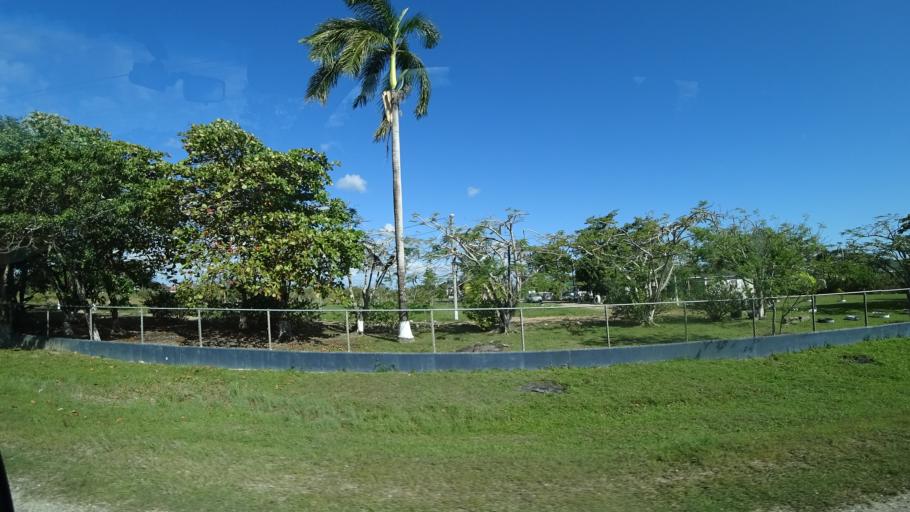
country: BZ
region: Belize
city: Belize City
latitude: 17.5820
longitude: -88.3592
